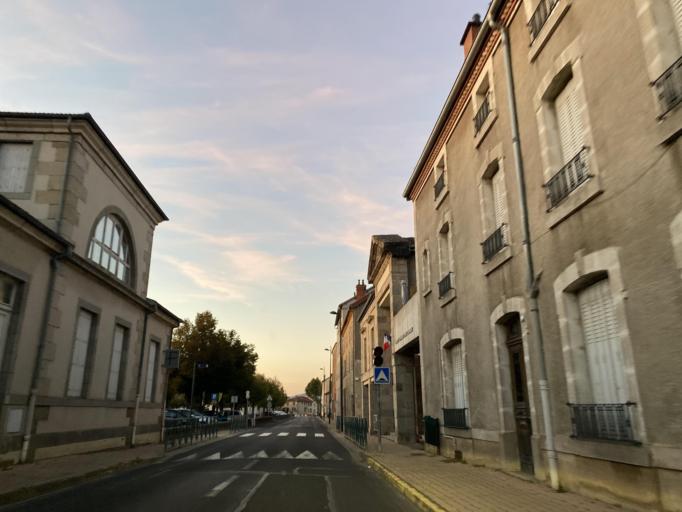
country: FR
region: Auvergne
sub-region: Departement du Puy-de-Dome
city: Ambert
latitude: 45.5469
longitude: 3.7455
